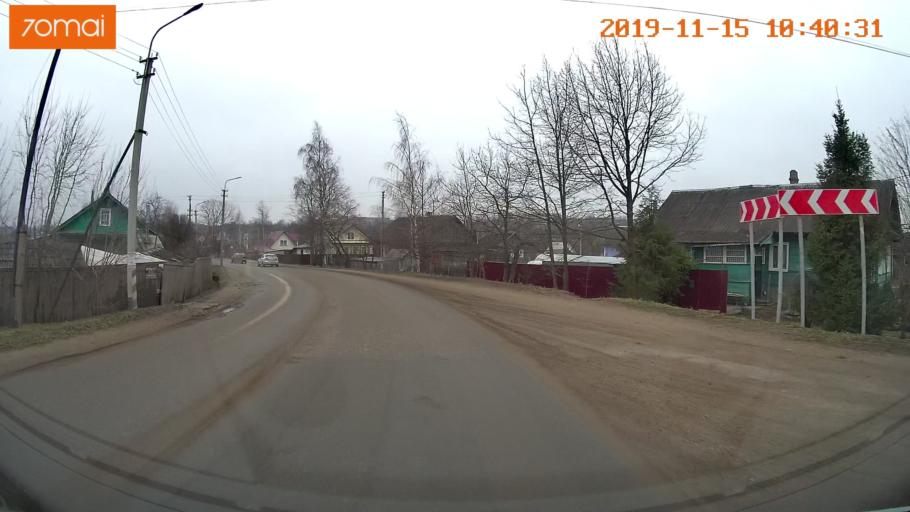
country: RU
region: Vologda
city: Sheksna
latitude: 59.2137
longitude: 38.5093
